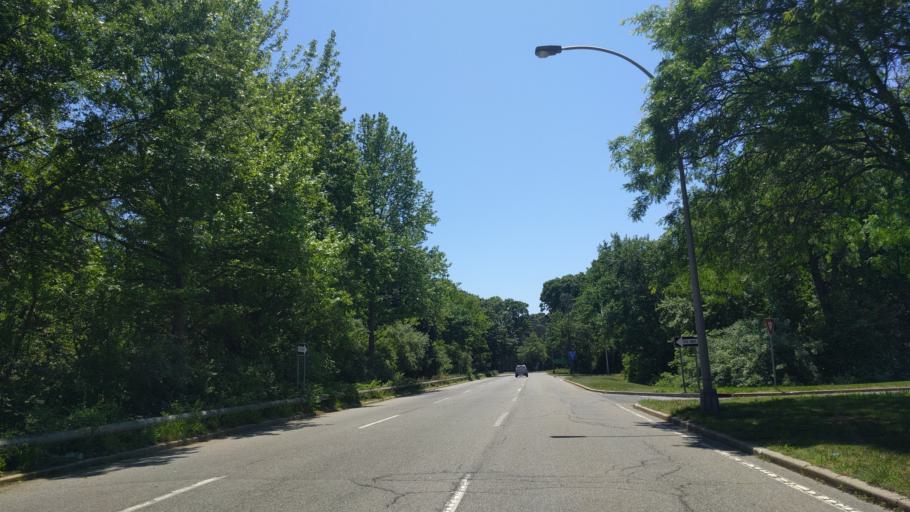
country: US
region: New York
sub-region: Suffolk County
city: Hauppauge
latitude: 40.8213
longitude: -73.2227
